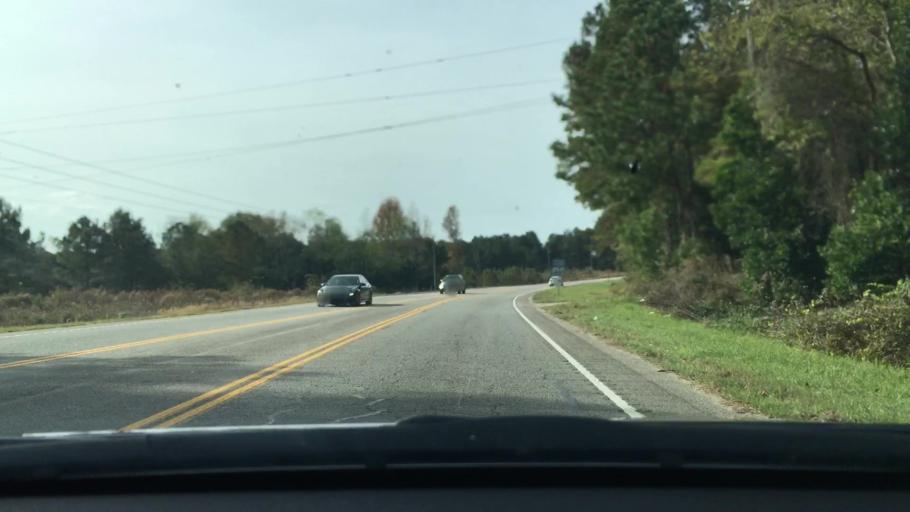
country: US
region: South Carolina
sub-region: Sumter County
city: Cherryvale
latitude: 33.9363
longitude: -80.4426
